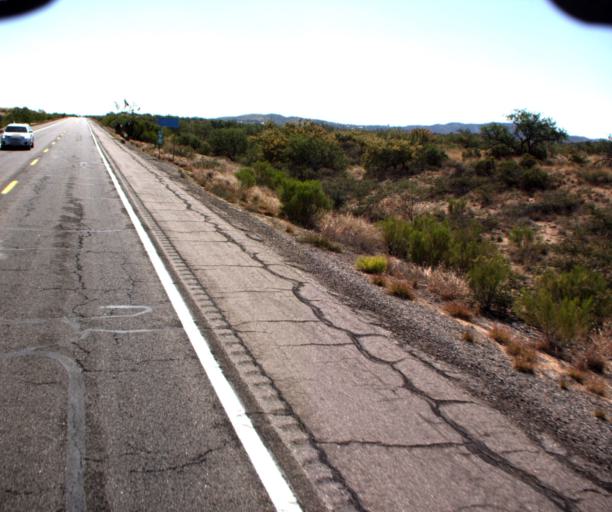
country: US
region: Arizona
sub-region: Pinal County
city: Oracle
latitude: 32.6122
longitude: -110.8399
